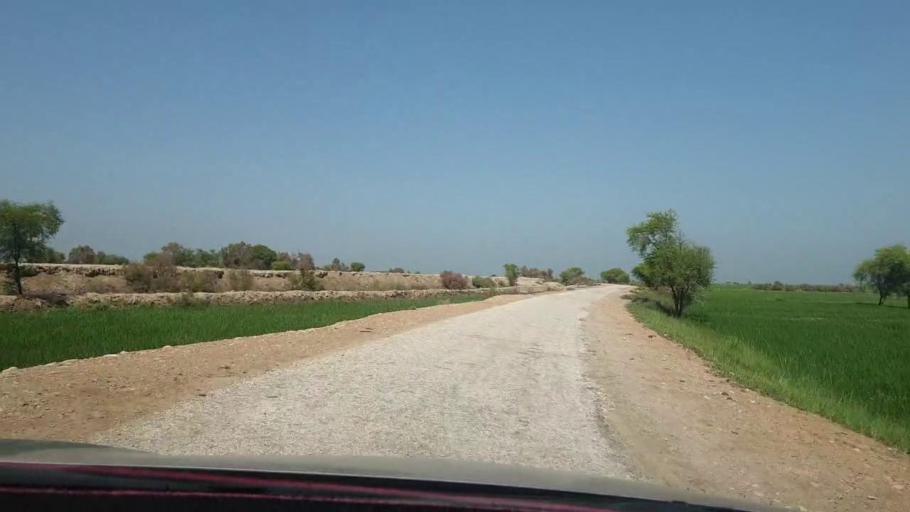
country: PK
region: Sindh
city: Warah
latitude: 27.5504
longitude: 67.7373
